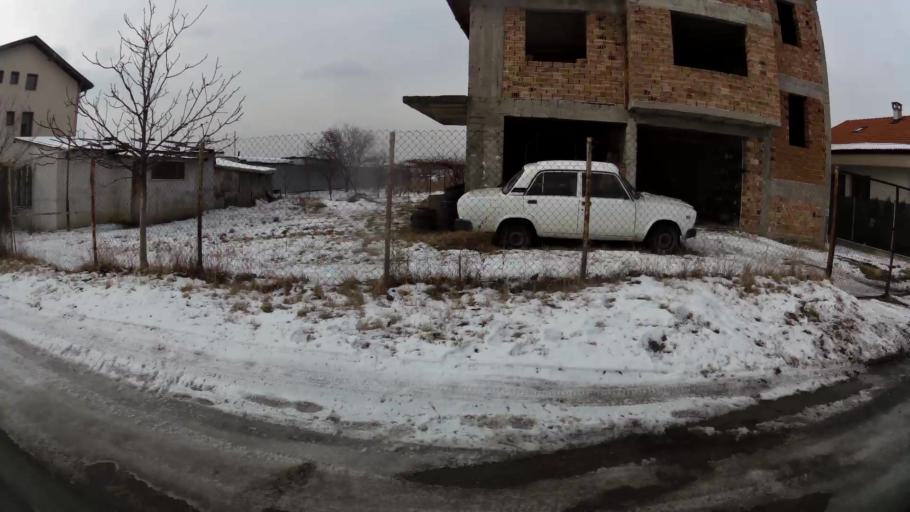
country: BG
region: Sofia-Capital
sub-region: Stolichna Obshtina
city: Sofia
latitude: 42.7136
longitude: 23.4002
